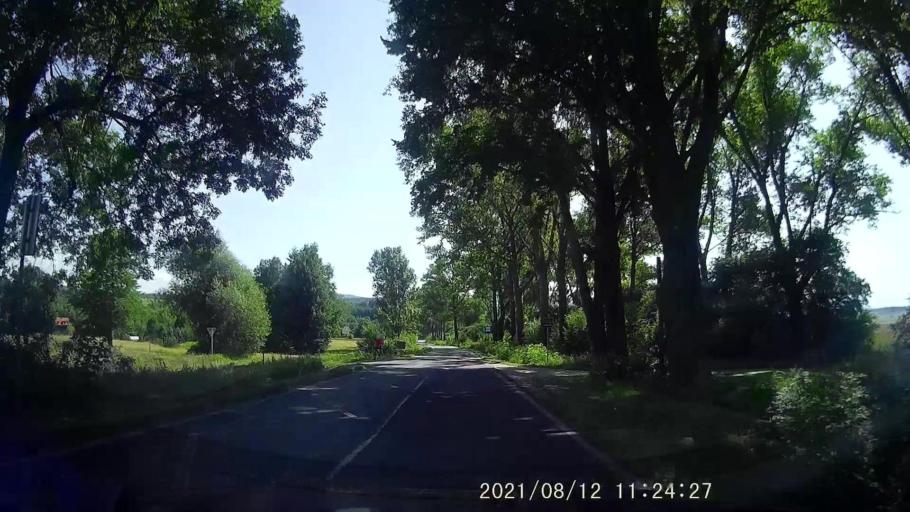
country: PL
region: Lower Silesian Voivodeship
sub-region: Powiat klodzki
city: Bystrzyca Klodzka
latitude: 50.2908
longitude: 16.6664
